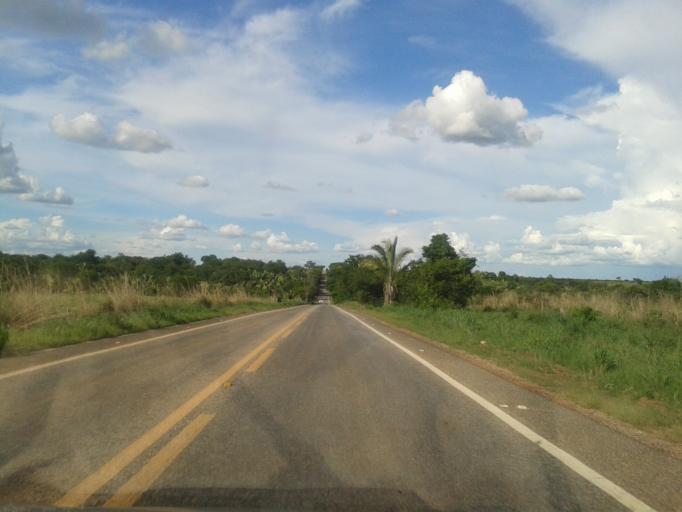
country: BR
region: Goias
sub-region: Mozarlandia
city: Mozarlandia
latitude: -14.4770
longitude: -50.4743
